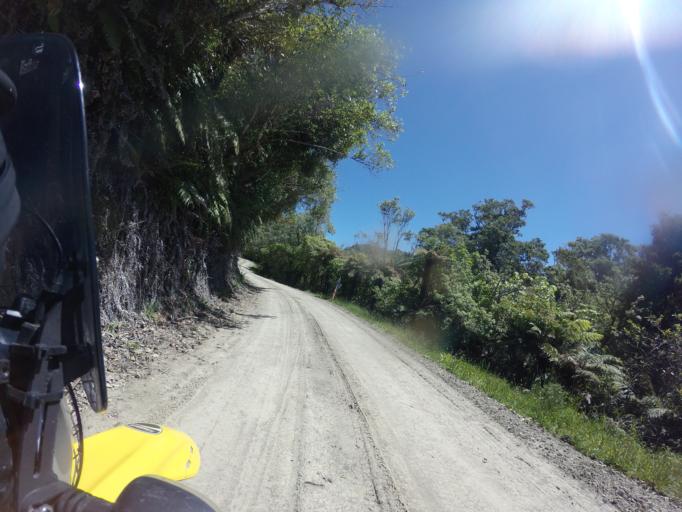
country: NZ
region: Bay of Plenty
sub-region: Opotiki District
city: Opotiki
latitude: -38.4086
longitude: 177.4243
